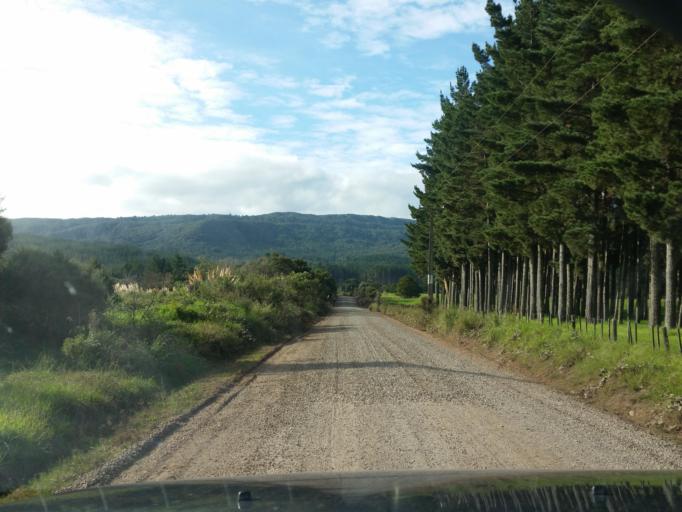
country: NZ
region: Northland
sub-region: Kaipara District
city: Dargaville
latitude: -35.7773
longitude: 173.7132
